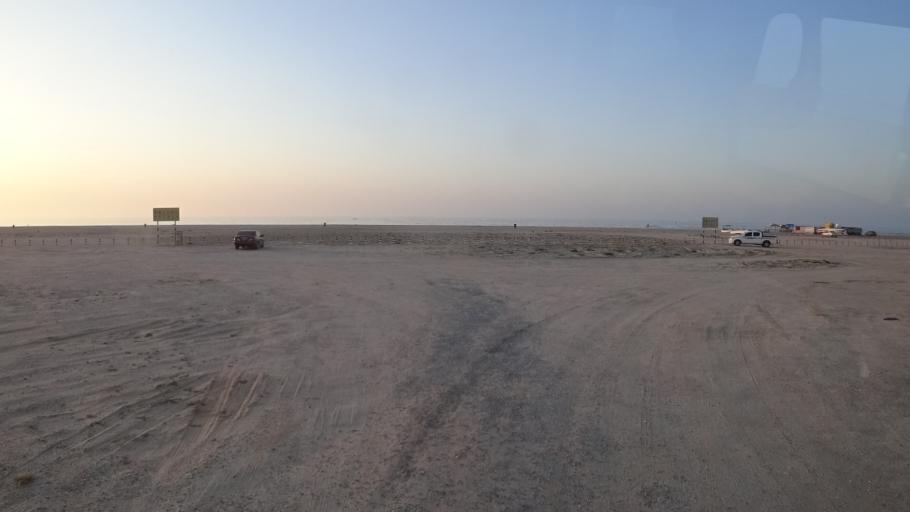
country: OM
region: Ash Sharqiyah
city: Sur
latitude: 22.5312
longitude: 59.7647
